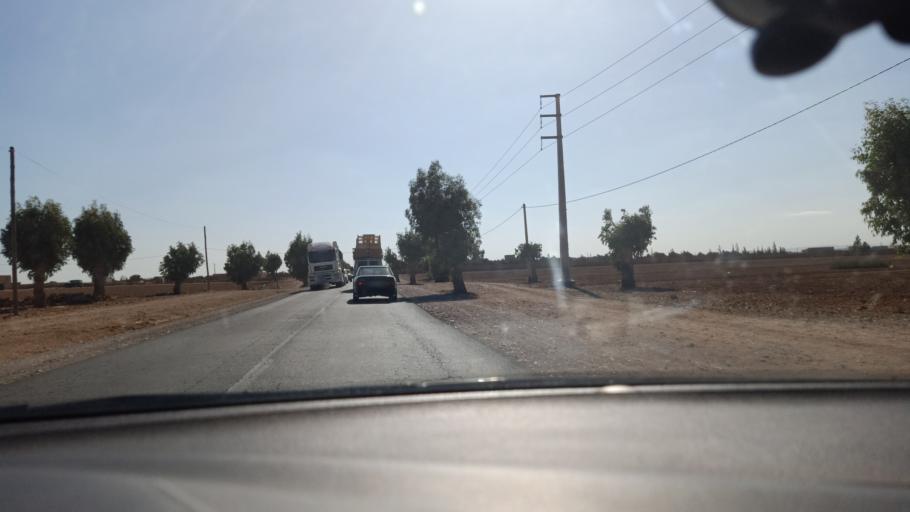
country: MA
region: Doukkala-Abda
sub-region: Safi
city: Youssoufia
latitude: 32.0975
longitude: -8.6142
